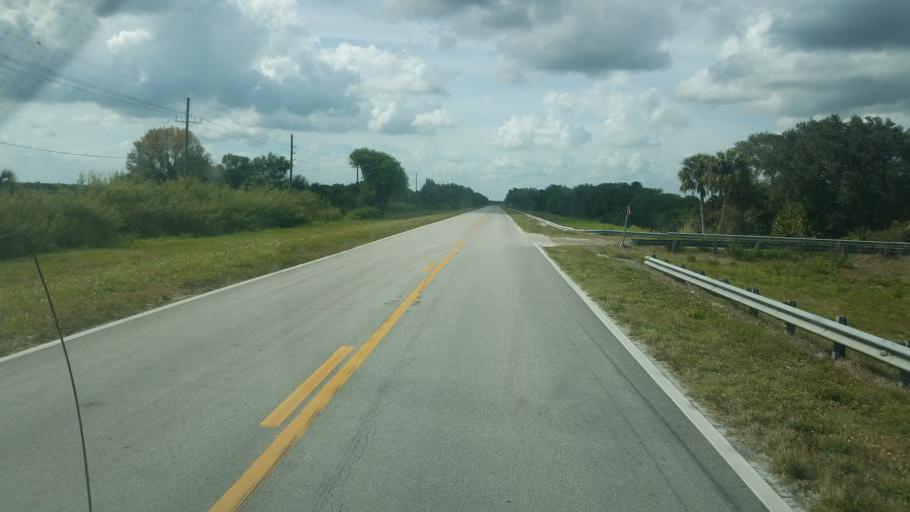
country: US
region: Florida
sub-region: Okeechobee County
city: Cypress Quarters
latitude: 27.4485
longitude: -80.6625
